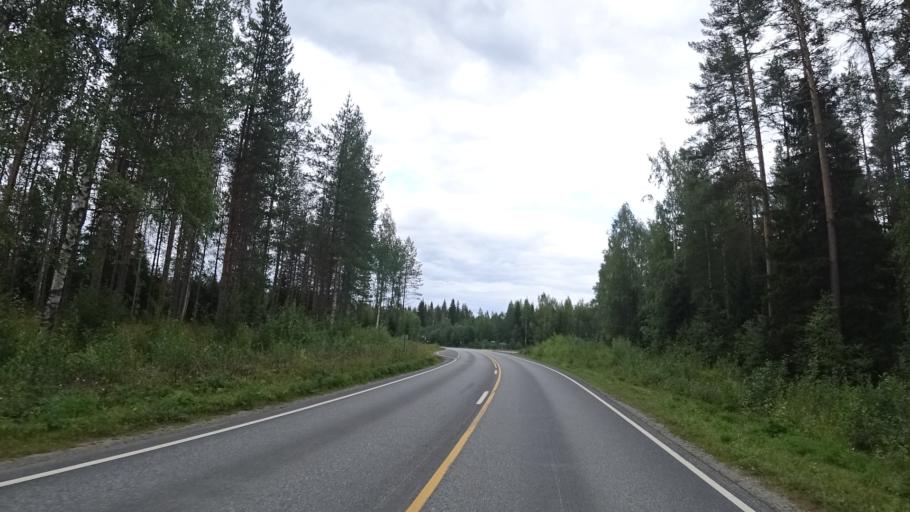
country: FI
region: North Karelia
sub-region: Joensuu
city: Ilomantsi
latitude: 62.6497
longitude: 30.9764
